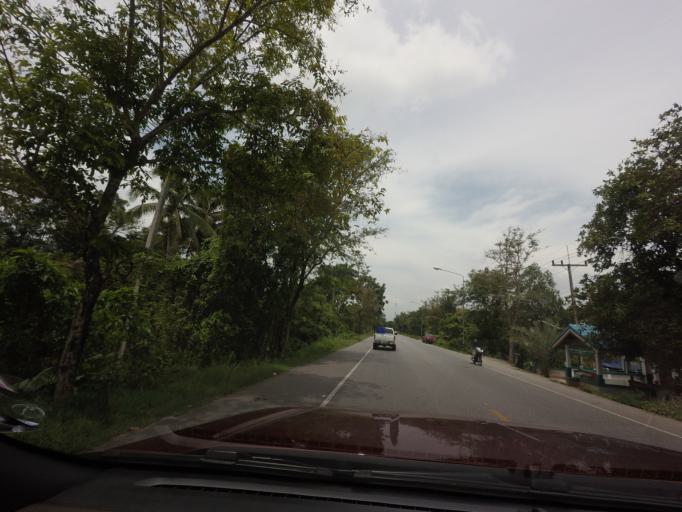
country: TH
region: Yala
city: Yala
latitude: 6.6162
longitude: 101.3061
